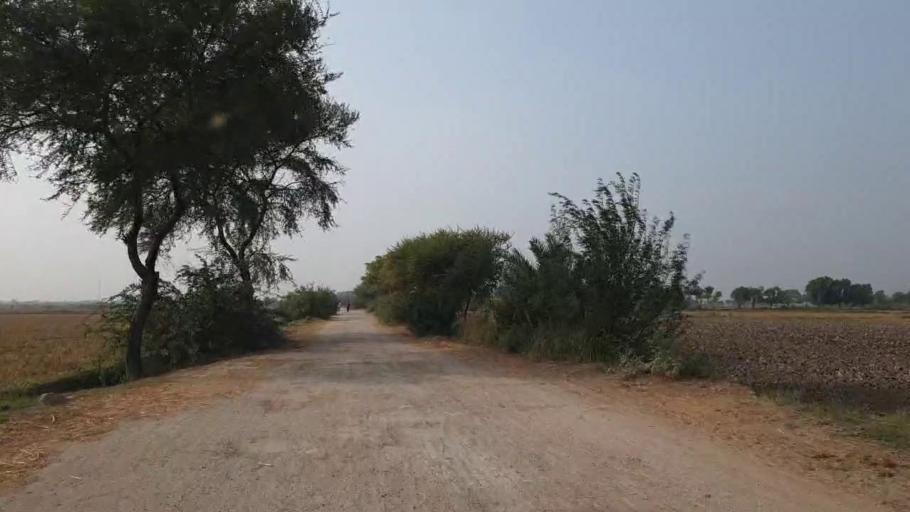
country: PK
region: Sindh
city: Matli
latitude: 25.0695
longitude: 68.5976
